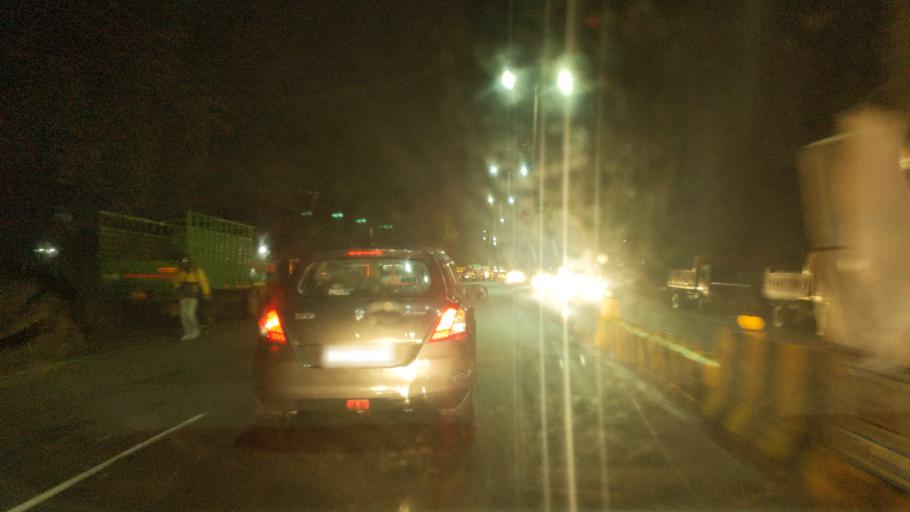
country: IN
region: Uttarakhand
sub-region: Naini Tal
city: Haldwani
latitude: 29.2534
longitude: 79.5416
